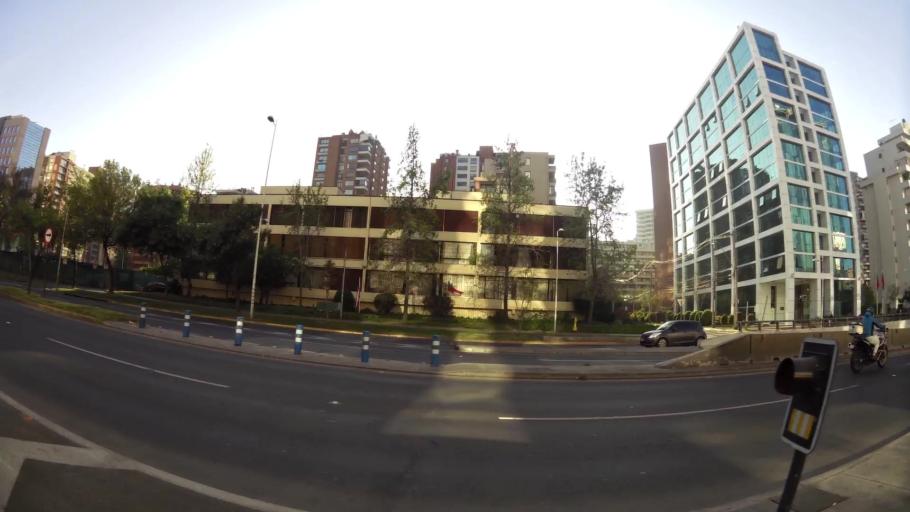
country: CL
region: Santiago Metropolitan
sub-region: Provincia de Santiago
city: Villa Presidente Frei, Nunoa, Santiago, Chile
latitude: -33.4068
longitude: -70.5683
